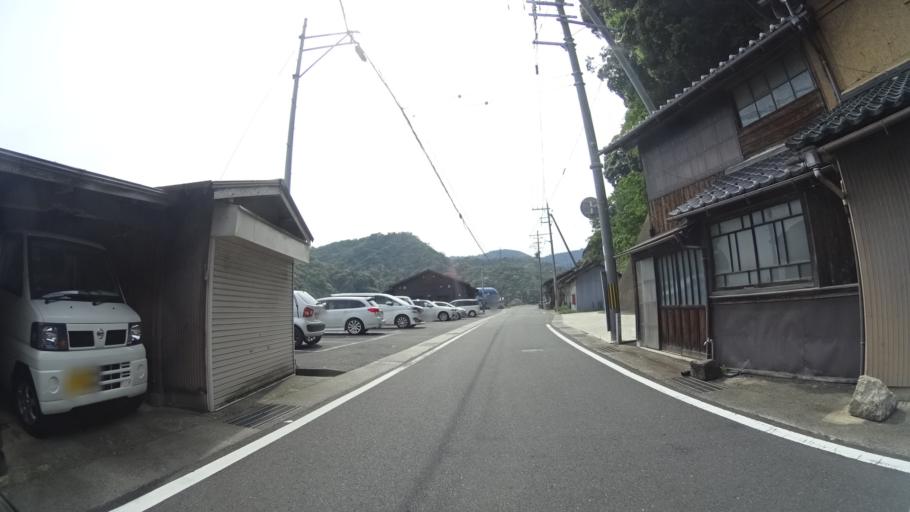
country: JP
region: Kyoto
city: Miyazu
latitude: 35.6700
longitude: 135.2781
